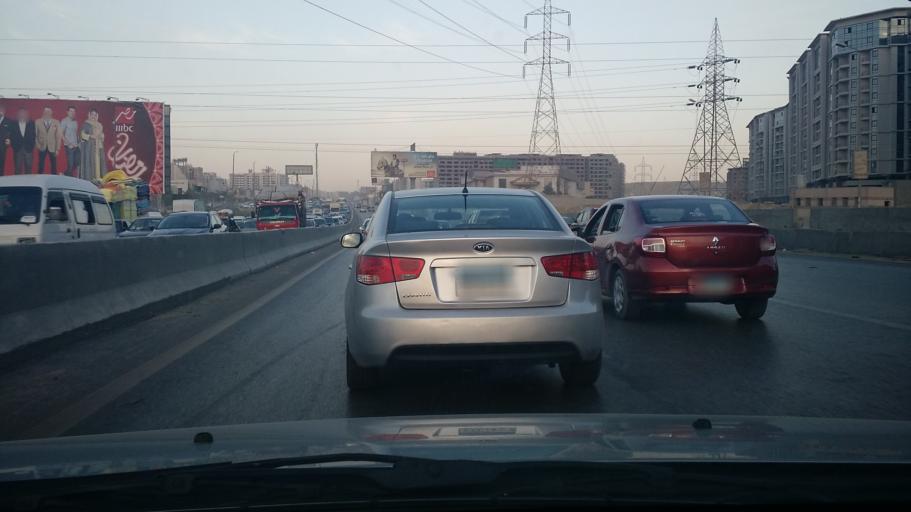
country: EG
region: Muhafazat al Qahirah
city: Cairo
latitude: 29.9837
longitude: 31.3251
